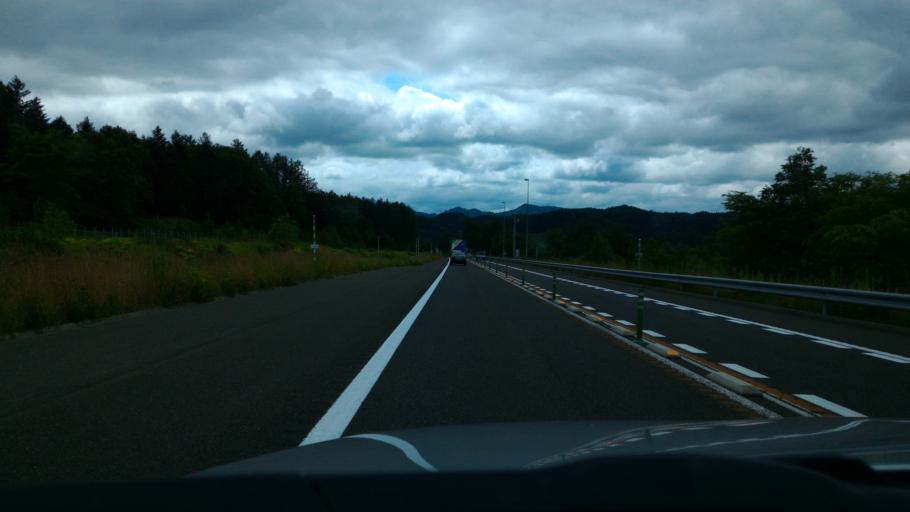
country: JP
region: Hokkaido
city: Shimo-furano
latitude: 42.9451
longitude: 142.2251
